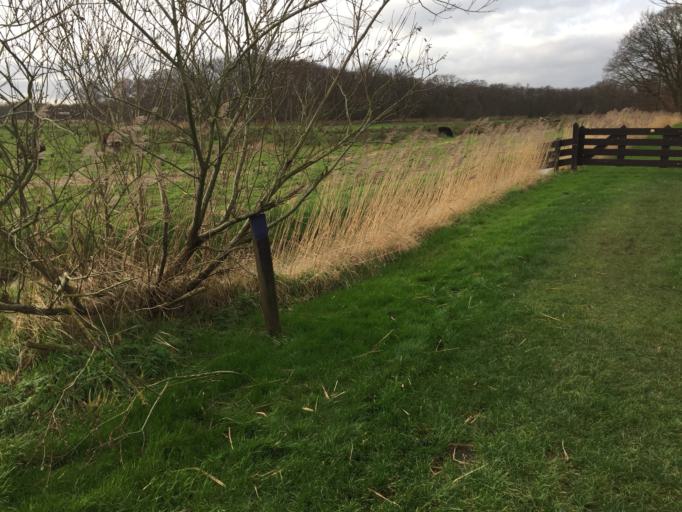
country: NL
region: North Holland
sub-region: Gemeente Bussum
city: Bussum
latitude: 52.2842
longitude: 5.1420
